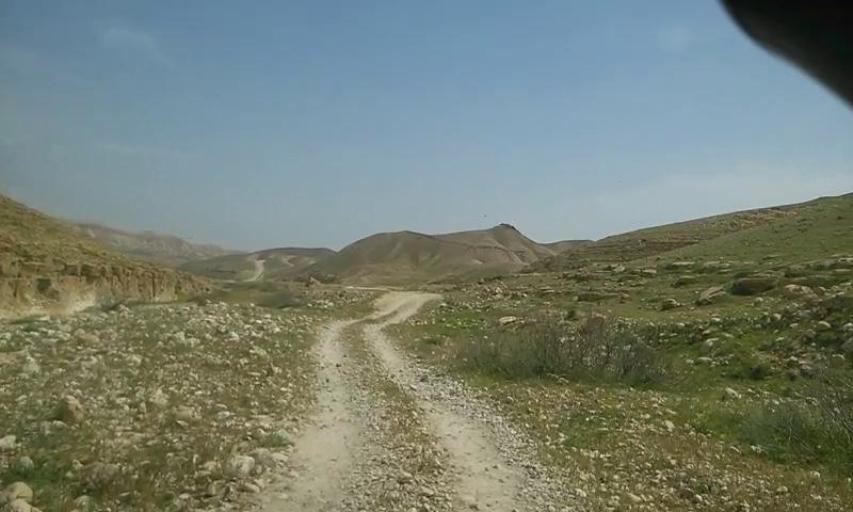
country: PS
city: `Arab ar Rashaydah
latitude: 31.5073
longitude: 35.2846
